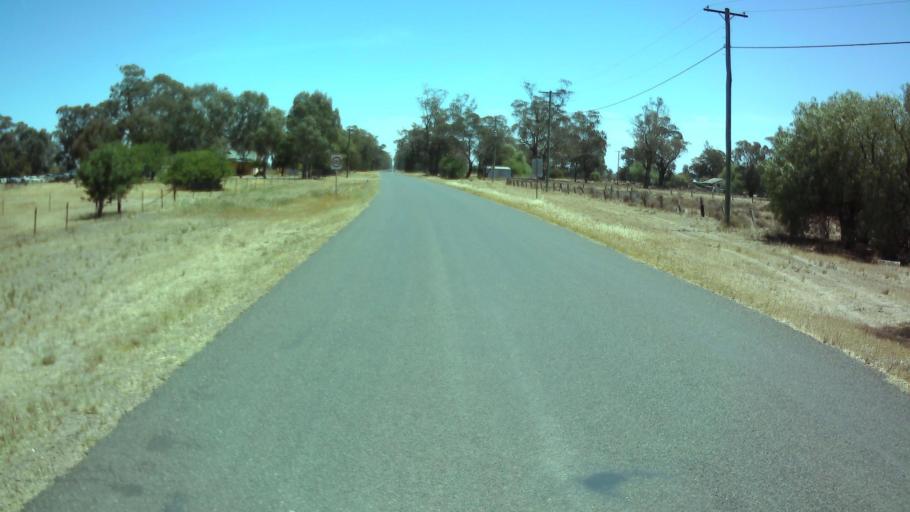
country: AU
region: New South Wales
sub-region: Weddin
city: Grenfell
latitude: -34.0381
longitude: 147.9264
